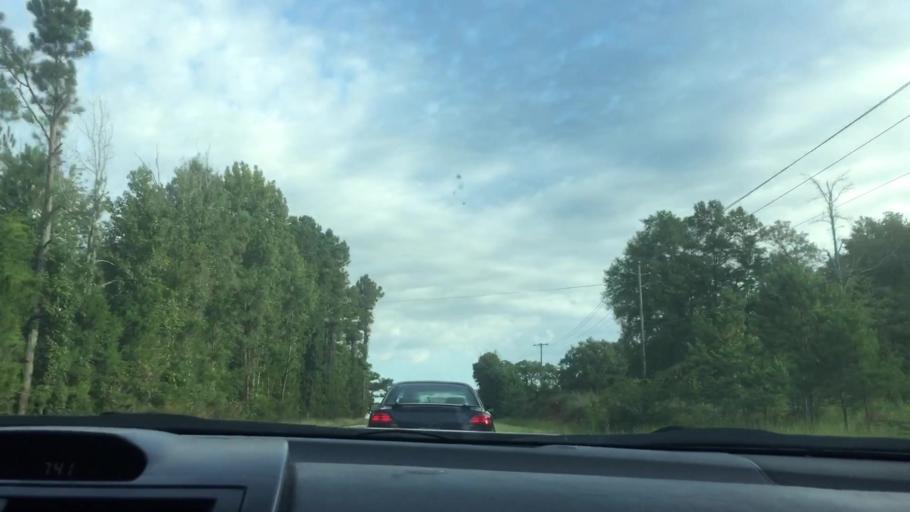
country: US
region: Alabama
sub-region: Hale County
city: Moundville
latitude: 32.9550
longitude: -87.6234
